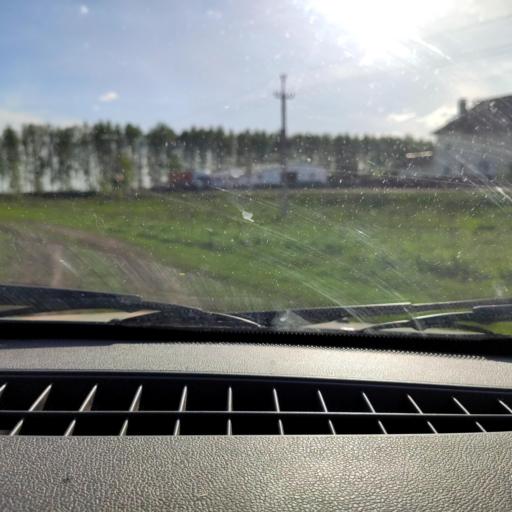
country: RU
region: Bashkortostan
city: Kabakovo
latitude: 54.6799
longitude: 56.1364
